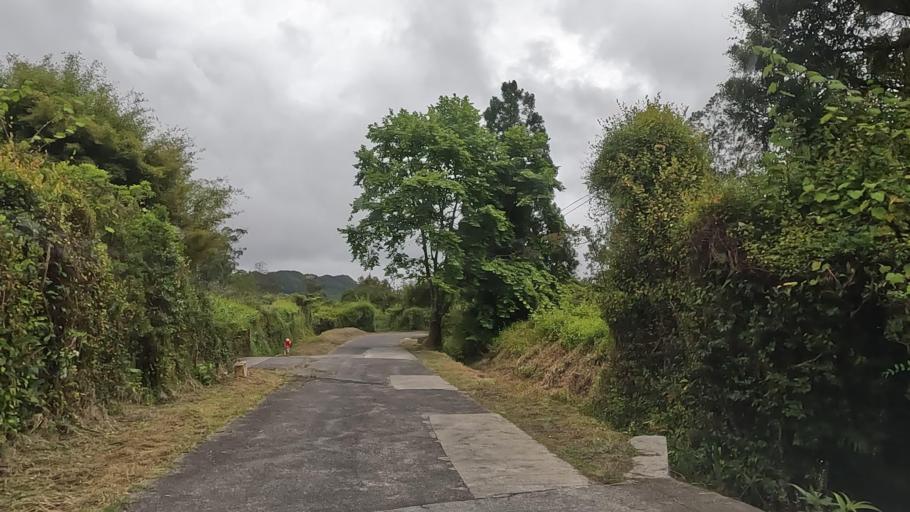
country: RE
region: Reunion
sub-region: Reunion
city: Saint-Benoit
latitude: -21.1203
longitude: 55.6387
